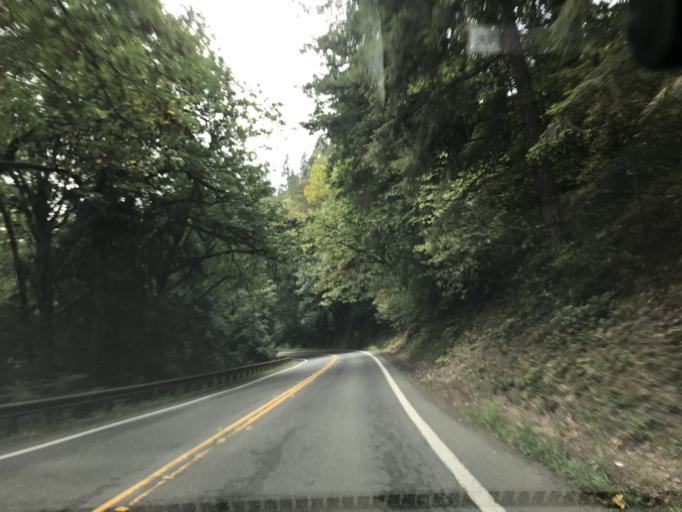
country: US
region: Washington
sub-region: King County
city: Black Diamond
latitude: 47.2840
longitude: -122.0363
